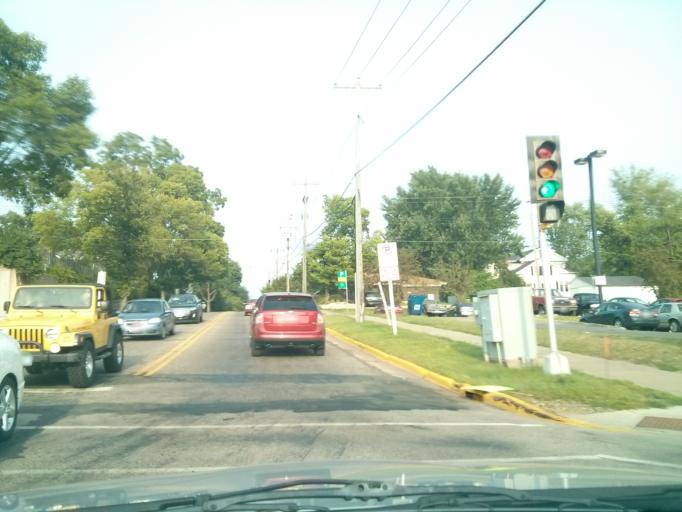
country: US
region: Wisconsin
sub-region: Saint Croix County
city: Hudson
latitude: 44.9770
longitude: -92.7571
